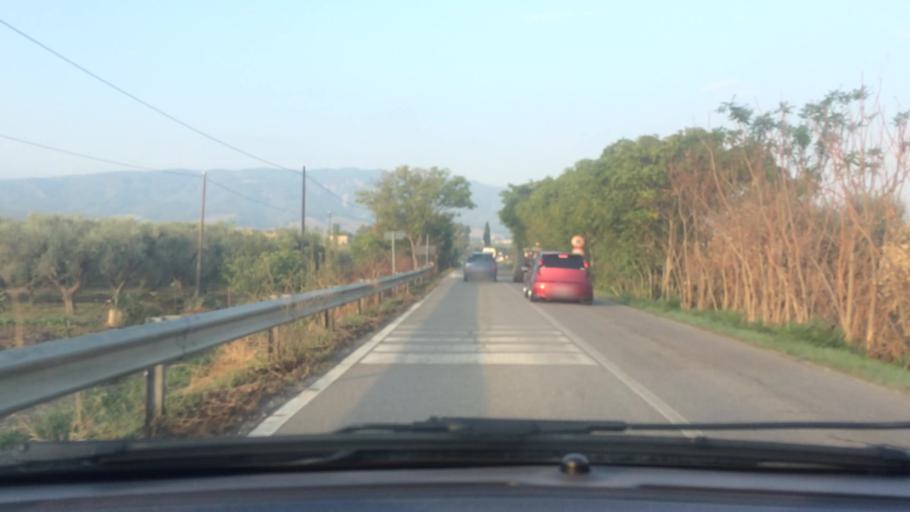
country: IT
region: Basilicate
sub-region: Provincia di Matera
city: Montescaglioso
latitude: 40.5330
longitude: 16.6417
